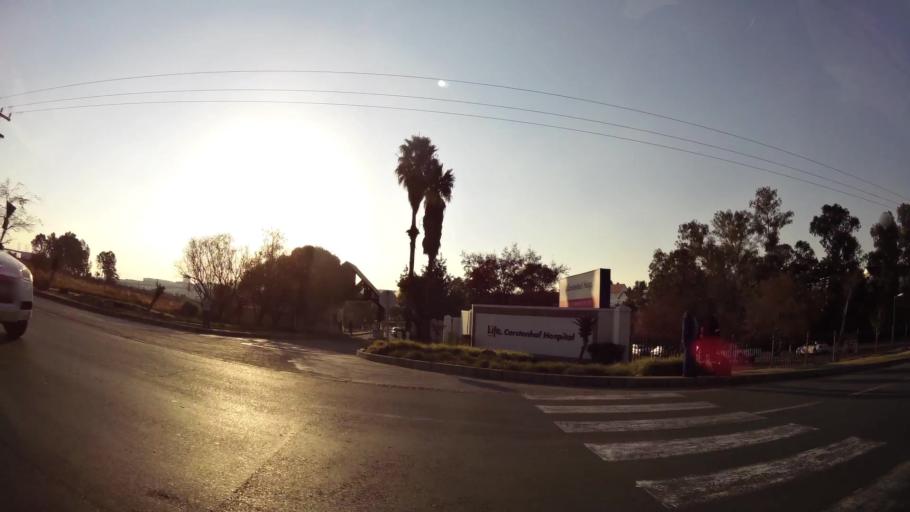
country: ZA
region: Gauteng
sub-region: City of Johannesburg Metropolitan Municipality
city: Midrand
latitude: -26.0313
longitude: 28.1396
